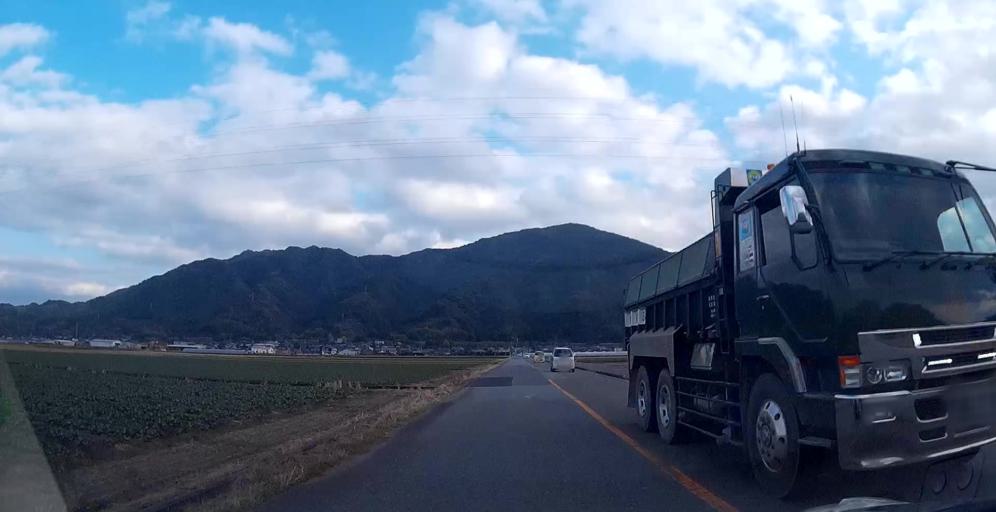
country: JP
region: Kumamoto
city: Yatsushiro
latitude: 32.5316
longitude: 130.6538
